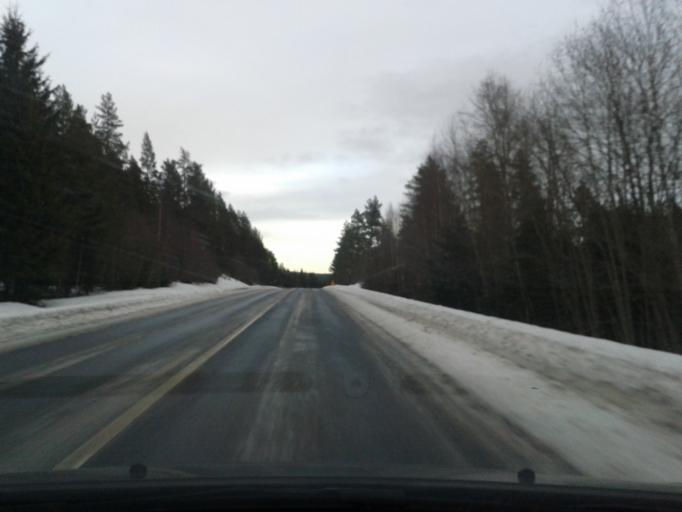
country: SE
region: Vaesternorrland
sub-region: Solleftea Kommun
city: Solleftea
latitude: 63.3328
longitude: 17.1067
